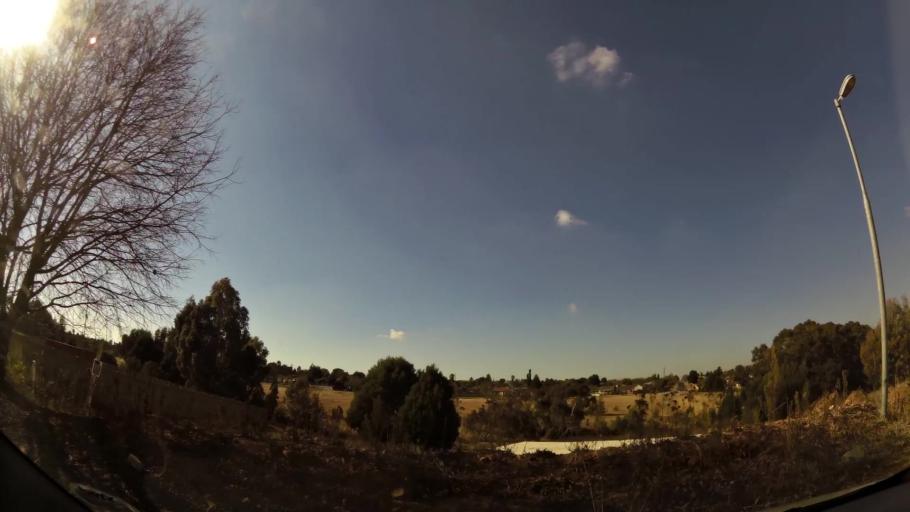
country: ZA
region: Gauteng
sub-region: City of Johannesburg Metropolitan Municipality
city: Roodepoort
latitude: -26.1372
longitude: 27.8216
